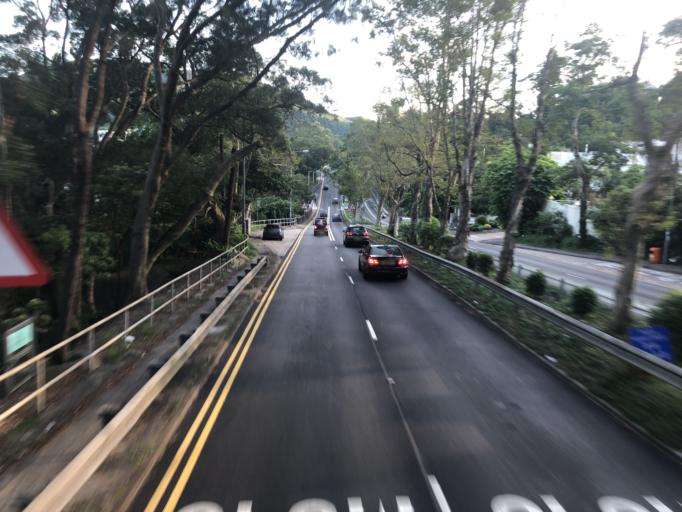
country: HK
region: Sai Kung
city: Sai Kung
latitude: 22.3373
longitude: 114.2431
